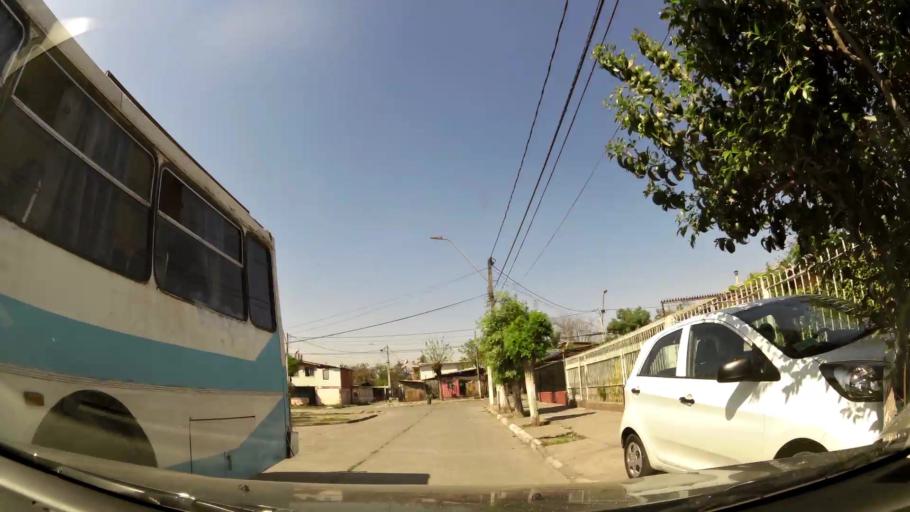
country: CL
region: Santiago Metropolitan
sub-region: Provincia de Maipo
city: San Bernardo
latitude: -33.5776
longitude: -70.7058
